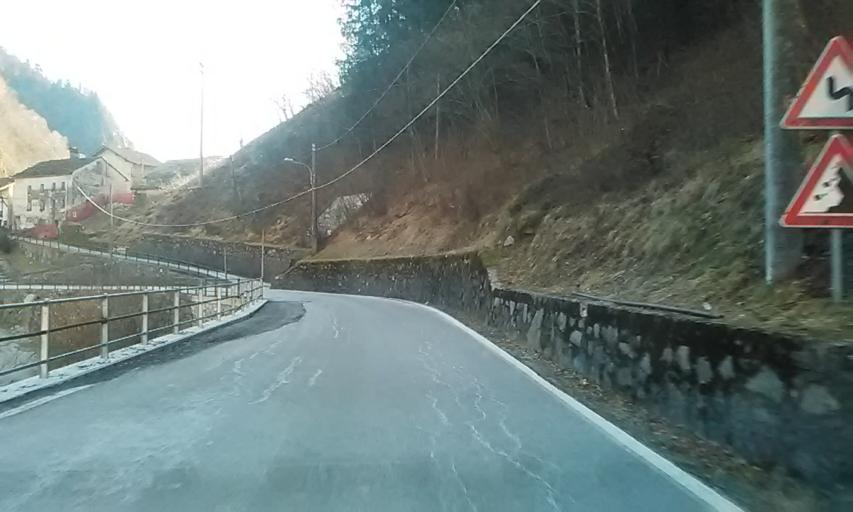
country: IT
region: Piedmont
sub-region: Provincia di Vercelli
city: Rimasco
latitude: 45.8558
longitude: 8.0631
